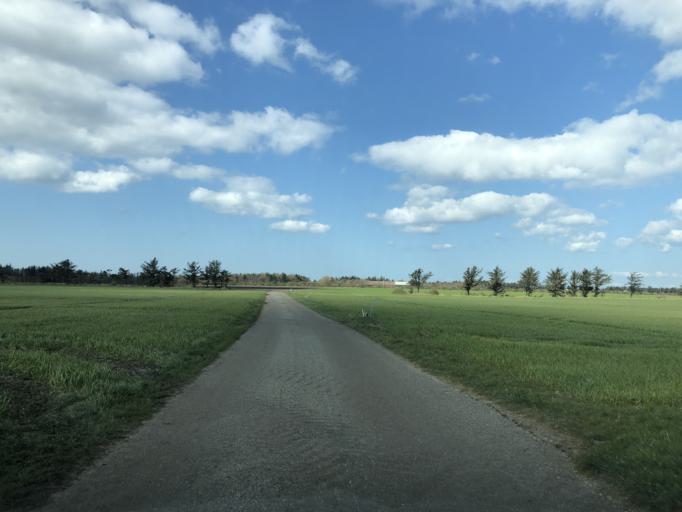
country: DK
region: Central Jutland
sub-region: Holstebro Kommune
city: Ulfborg
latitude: 56.3936
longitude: 8.1877
